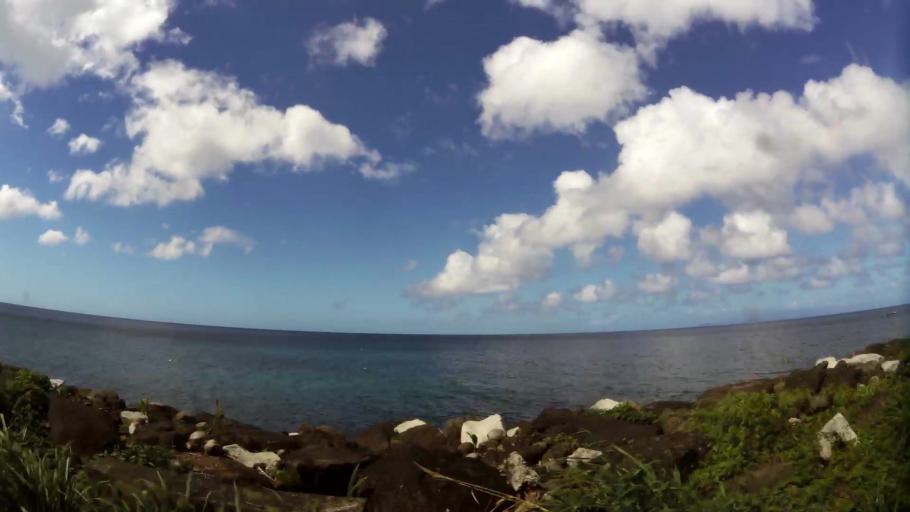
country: DM
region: Saint John
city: Portsmouth
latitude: 15.6271
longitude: -61.4641
